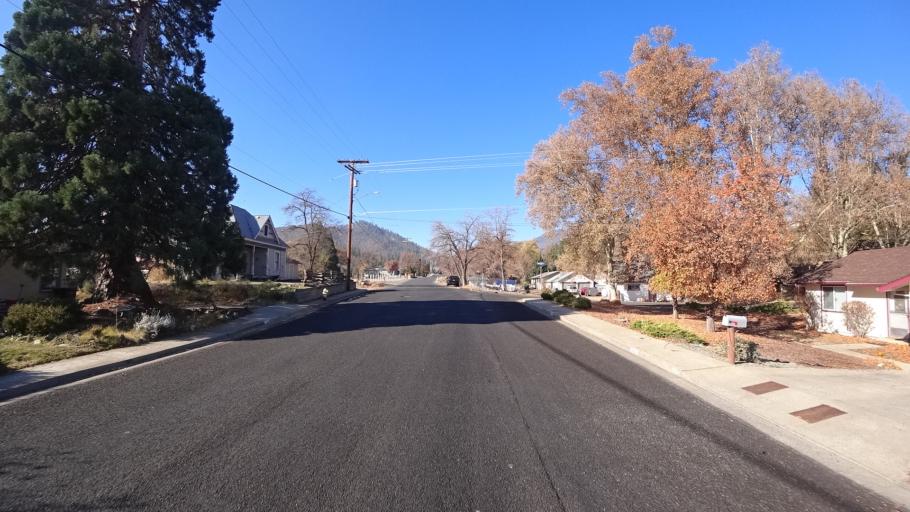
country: US
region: California
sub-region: Siskiyou County
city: Yreka
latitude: 41.7318
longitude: -122.6461
